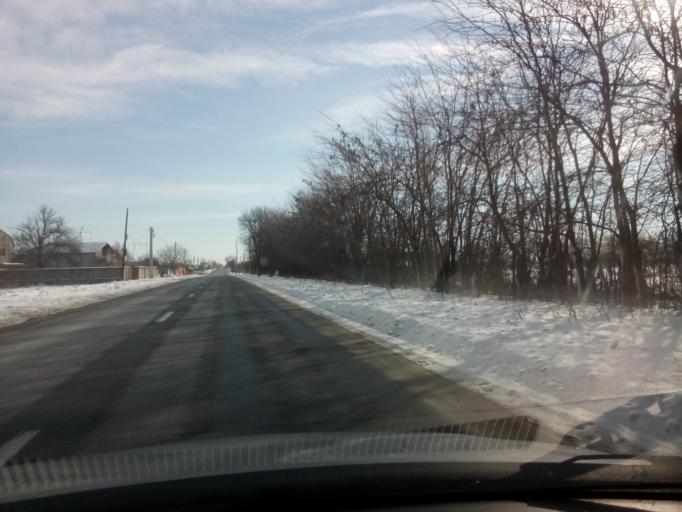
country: RO
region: Calarasi
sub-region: Comuna Frumusani
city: Frumusani
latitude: 44.3182
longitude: 26.2738
